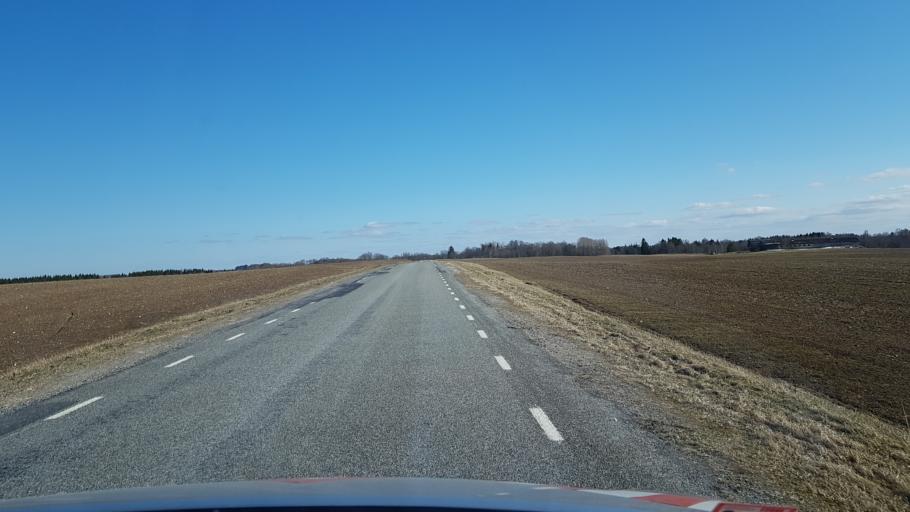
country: EE
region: Laeaene-Virumaa
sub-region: Kadrina vald
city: Kadrina
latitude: 59.3805
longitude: 26.0303
